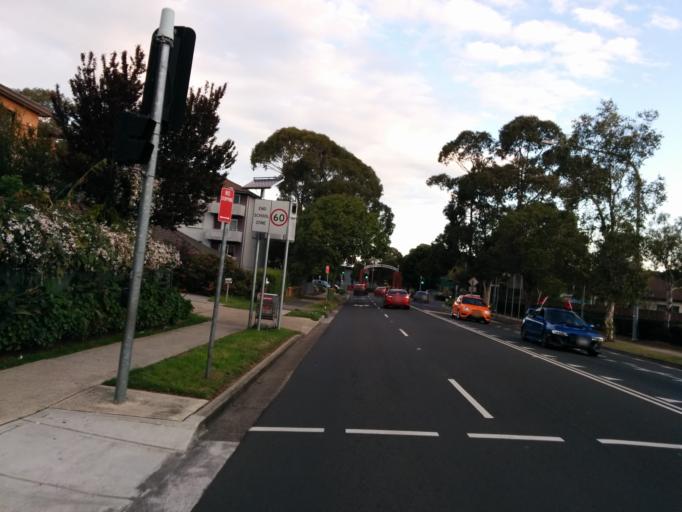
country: AU
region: New South Wales
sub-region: Fairfield
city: Carramar
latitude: -33.8733
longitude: 150.9591
